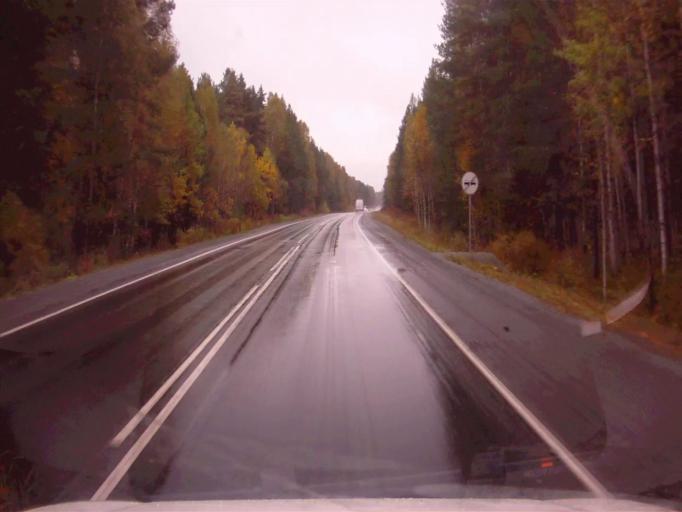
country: RU
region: Chelyabinsk
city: Tayginka
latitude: 55.5588
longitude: 60.6467
